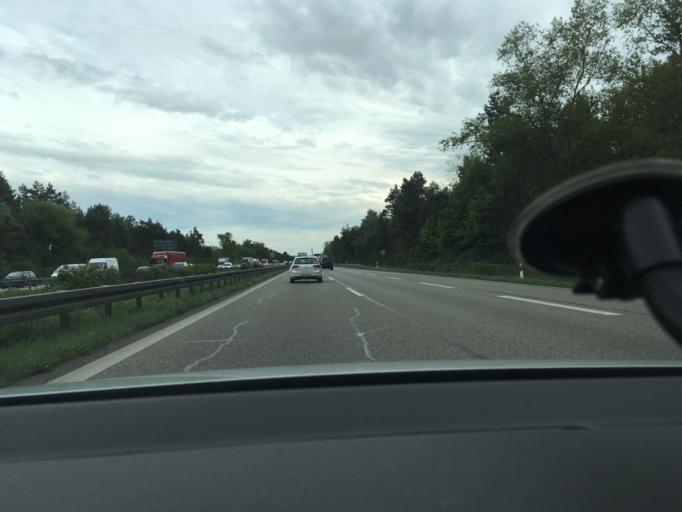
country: FR
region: Alsace
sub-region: Departement du Haut-Rhin
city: Fessenheim
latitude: 47.9041
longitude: 7.5875
